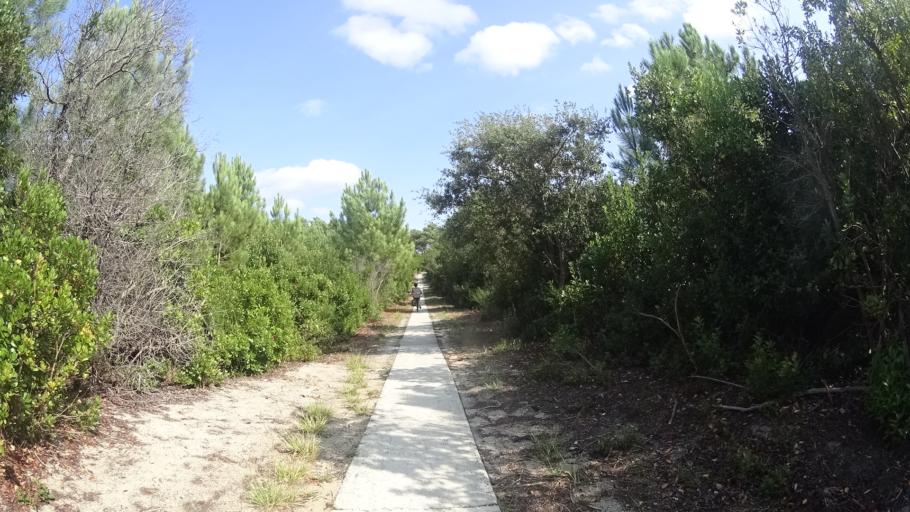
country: FR
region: Aquitaine
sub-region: Departement de la Gironde
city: Lacanau
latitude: 44.9654
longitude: -1.1759
